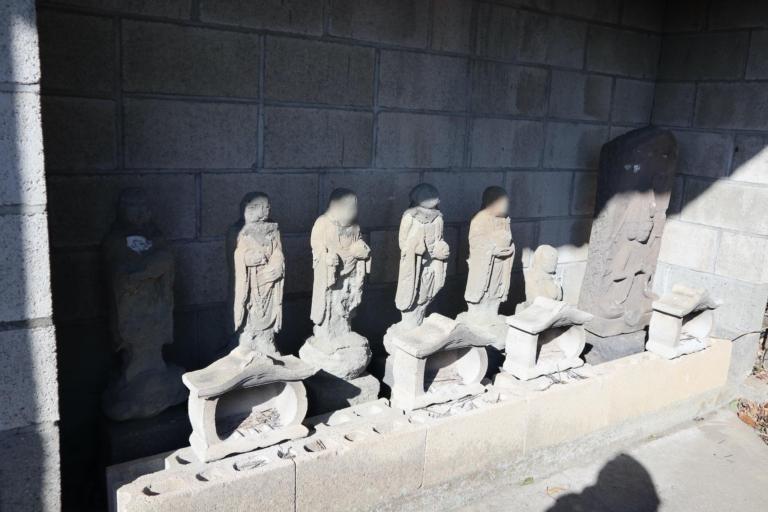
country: JP
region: Saitama
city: Fukiage-fujimi
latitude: 36.0909
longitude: 139.4443
